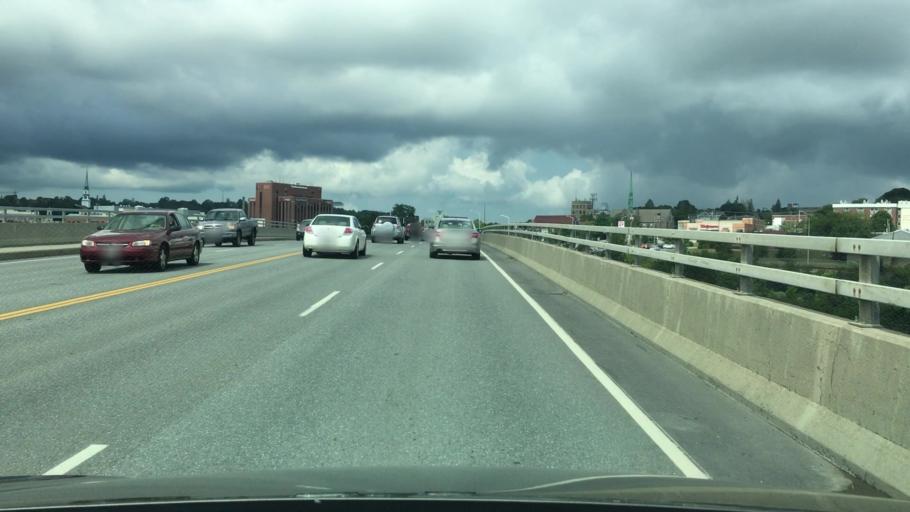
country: US
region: Maine
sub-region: Penobscot County
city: Brewer
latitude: 44.7987
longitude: -68.7634
